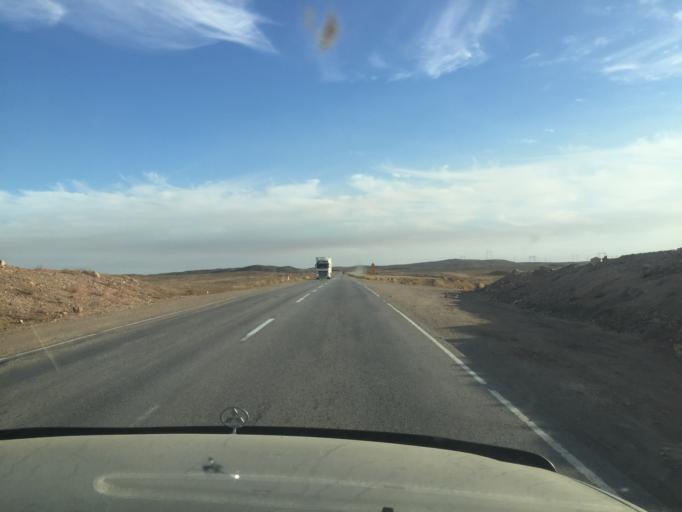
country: KZ
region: Zhambyl
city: Mynaral
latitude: 45.5220
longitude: 73.4873
